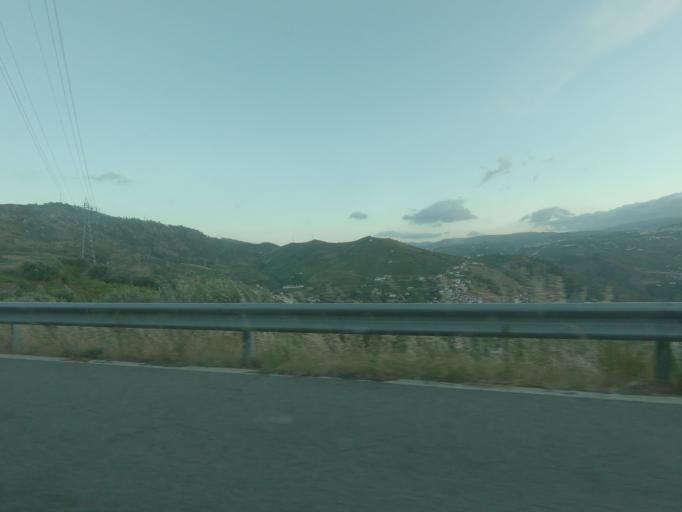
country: PT
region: Vila Real
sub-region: Peso da Regua
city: Peso da Regua
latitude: 41.1361
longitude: -7.7573
